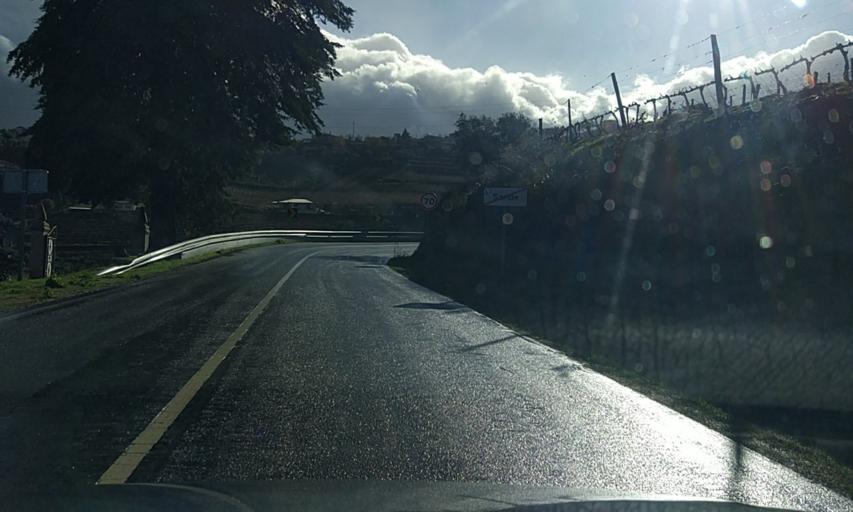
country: PT
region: Viseu
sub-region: Lamego
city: Lamego
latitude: 41.1220
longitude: -7.7935
